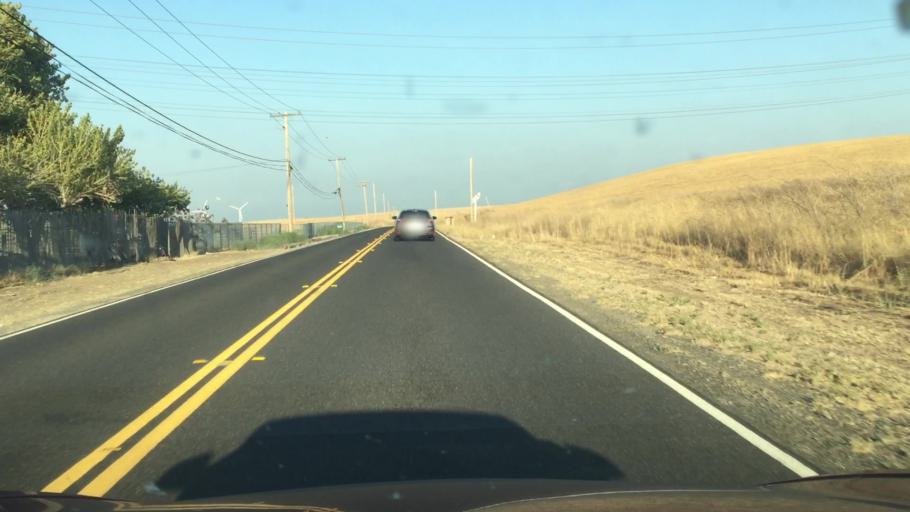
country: US
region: California
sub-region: San Joaquin County
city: Mountain House
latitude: 37.7135
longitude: -121.5517
